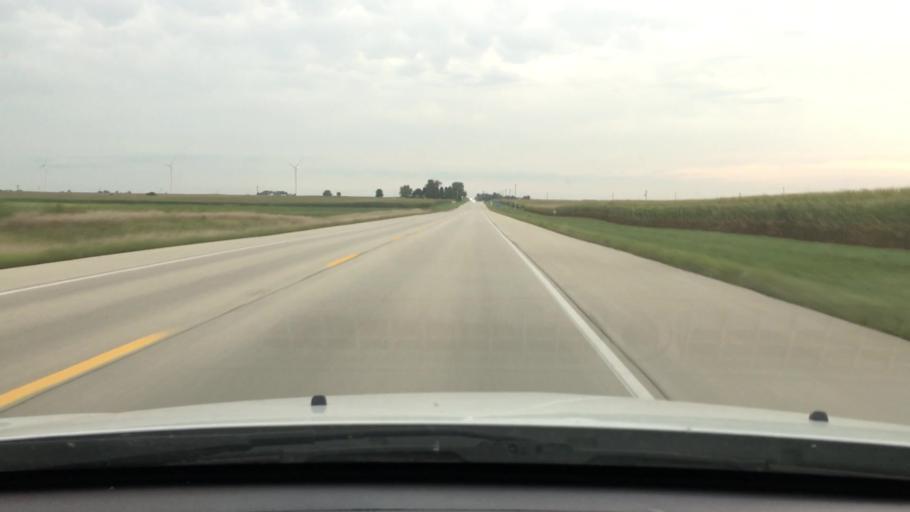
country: US
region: Illinois
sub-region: DeKalb County
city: Waterman
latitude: 41.8023
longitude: -88.7540
